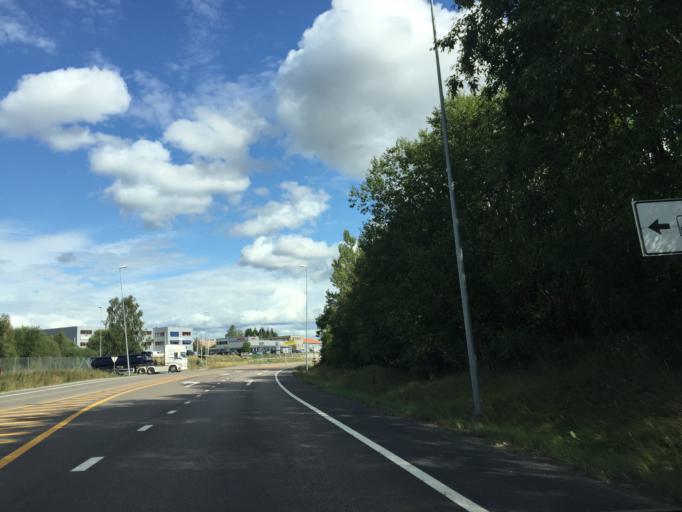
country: NO
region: Ostfold
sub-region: Hobol
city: Knappstad
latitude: 59.6169
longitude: 11.0540
